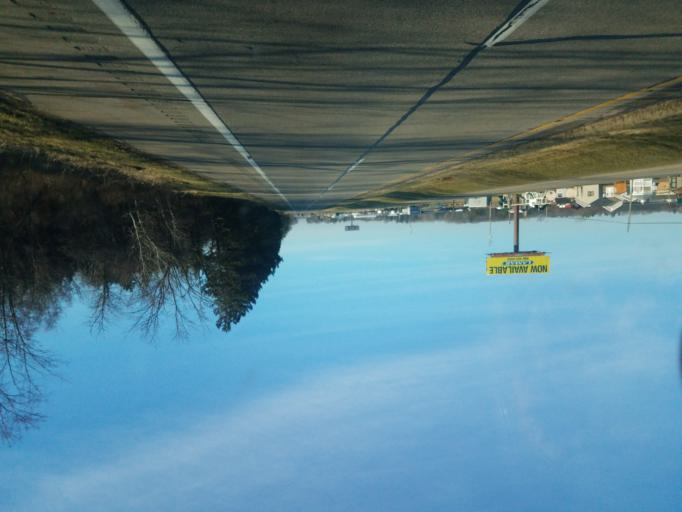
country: US
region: Michigan
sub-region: Clinton County
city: Saint Johns
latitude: 43.0900
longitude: -84.5635
